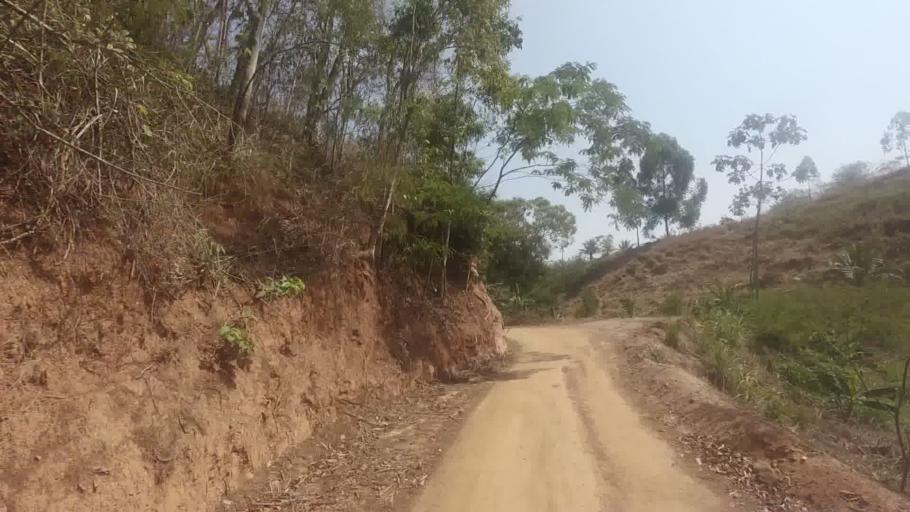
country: BR
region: Espirito Santo
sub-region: Sao Jose Do Calcado
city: Sao Jose do Calcado
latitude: -21.0020
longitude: -41.5068
